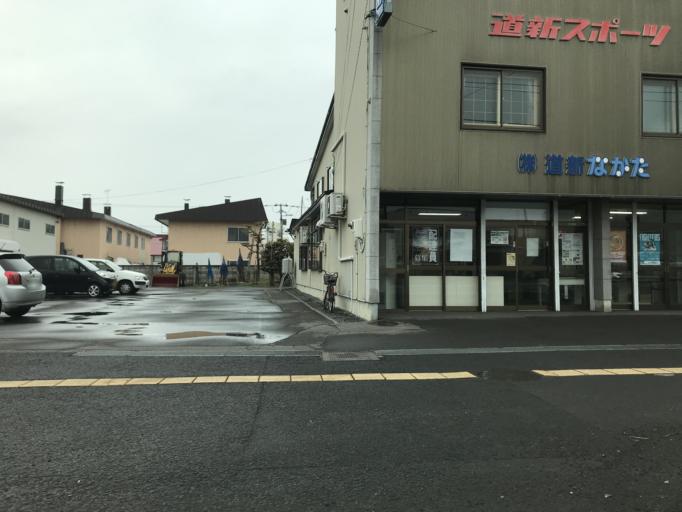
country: JP
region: Hokkaido
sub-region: Asahikawa-shi
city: Asahikawa
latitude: 43.7634
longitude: 142.3472
